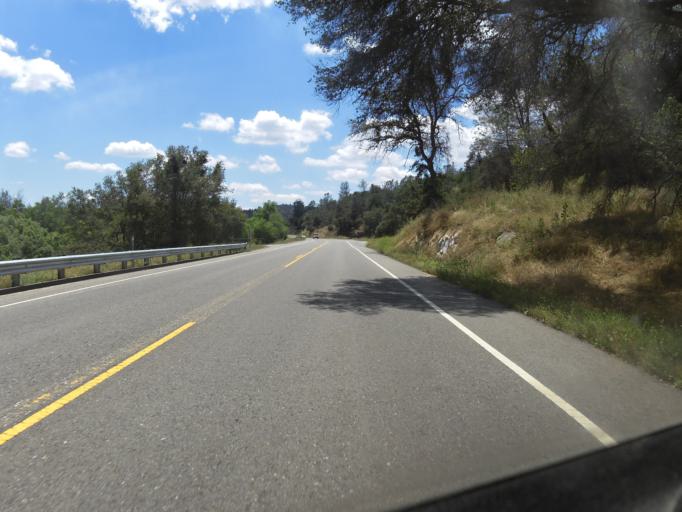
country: US
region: California
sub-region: Madera County
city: Coarsegold
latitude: 37.1677
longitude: -119.6387
